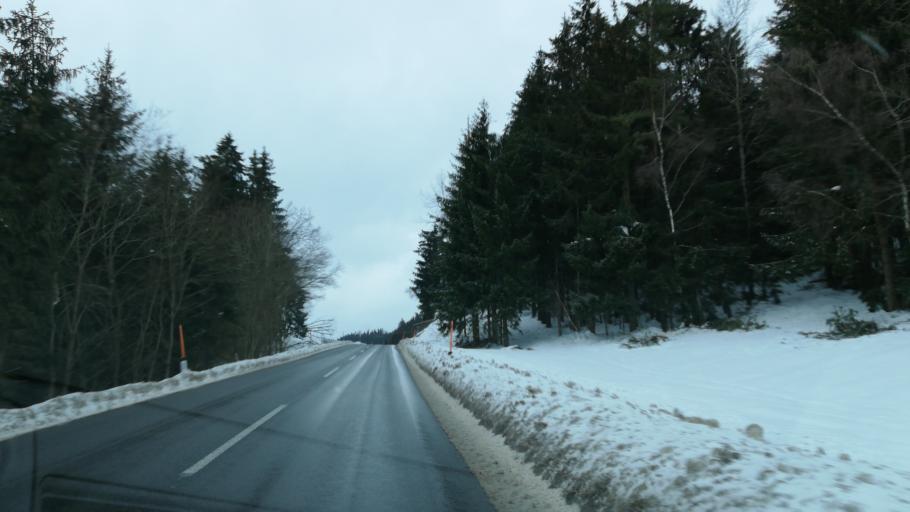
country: AT
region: Upper Austria
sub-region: Politischer Bezirk Urfahr-Umgebung
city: Herzogsdorf
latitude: 48.4694
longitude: 14.1395
